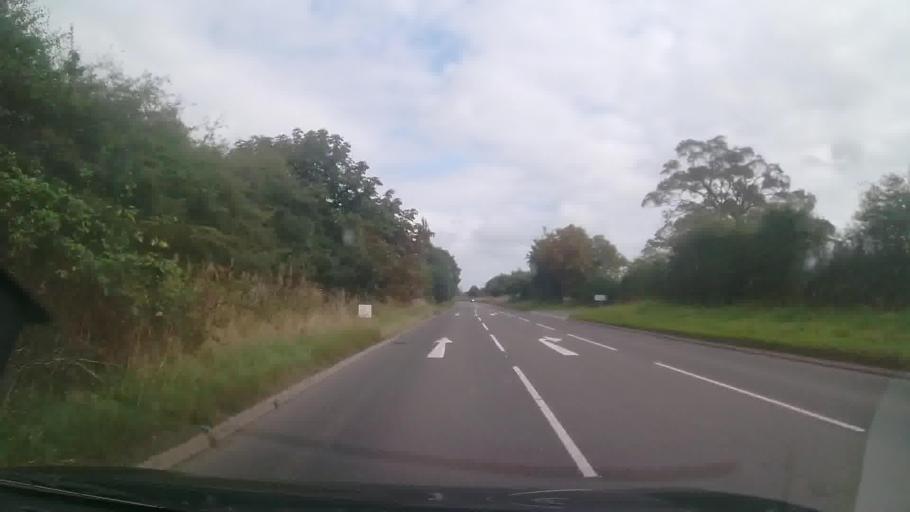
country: GB
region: England
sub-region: Shropshire
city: Whitchurch
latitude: 52.9625
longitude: -2.6647
